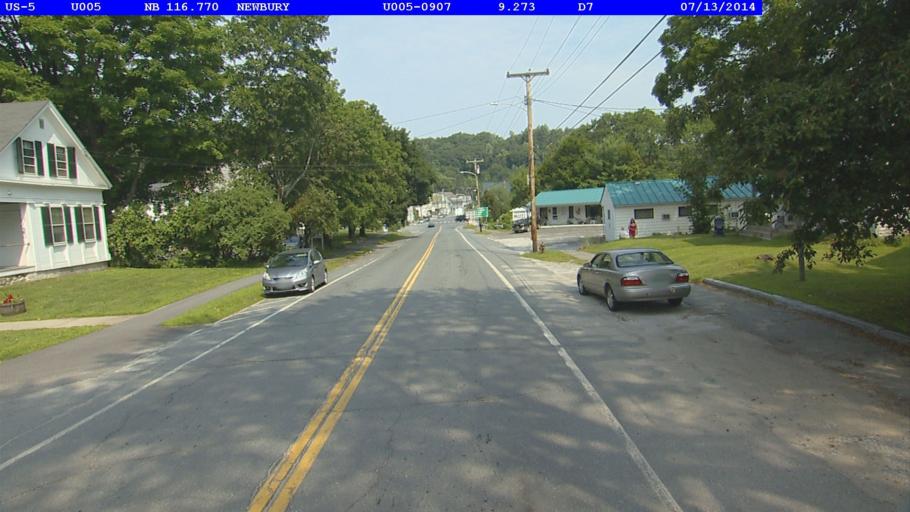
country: US
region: New Hampshire
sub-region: Grafton County
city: Woodsville
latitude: 44.1513
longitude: -72.0449
